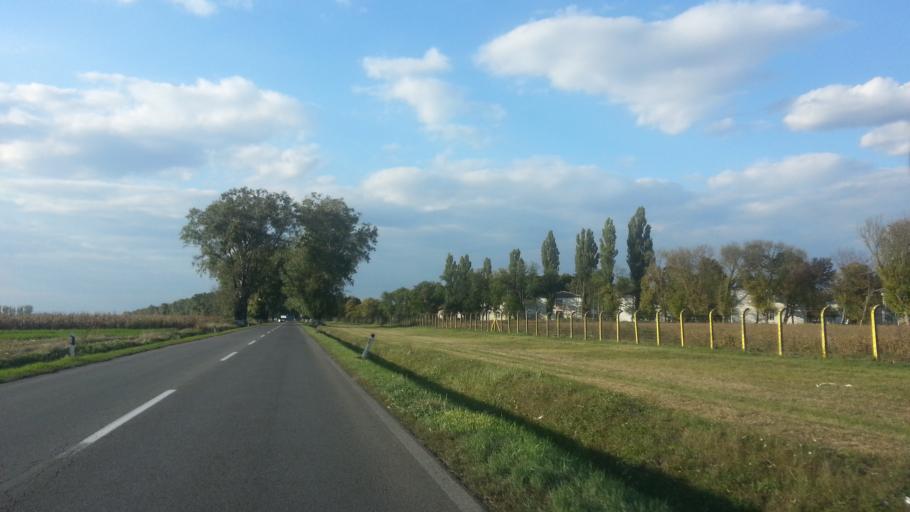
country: RS
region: Autonomna Pokrajina Vojvodina
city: Nova Pazova
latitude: 44.9223
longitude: 20.2496
